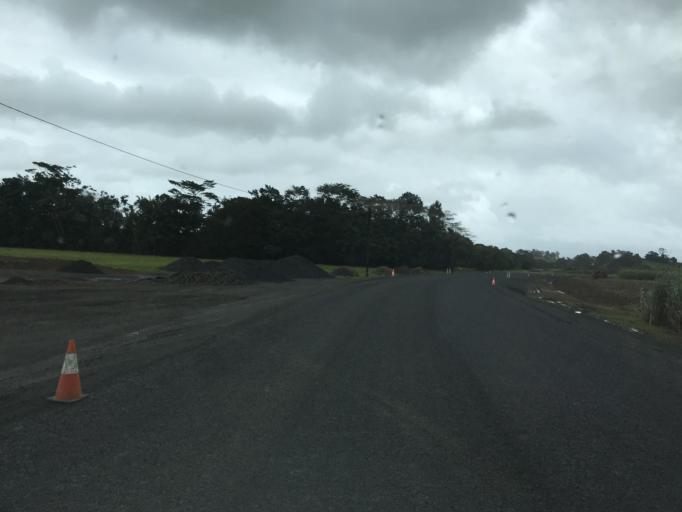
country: AU
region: Queensland
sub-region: Cassowary Coast
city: Innisfail
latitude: -17.5032
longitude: 145.9922
